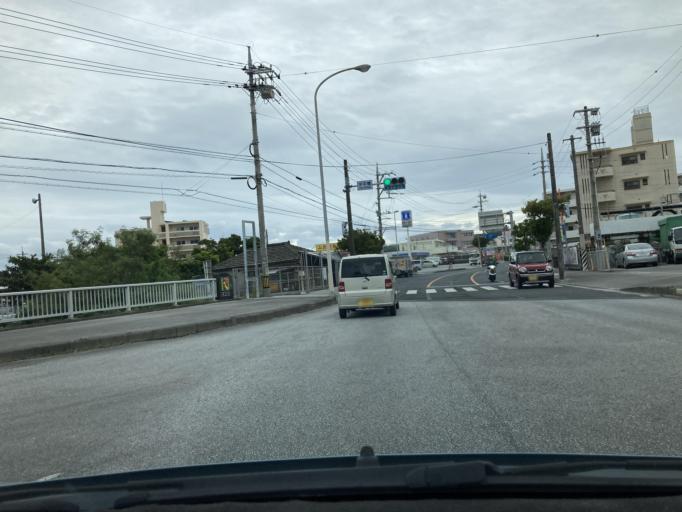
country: JP
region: Okinawa
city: Tomigusuku
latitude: 26.1790
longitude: 127.7180
